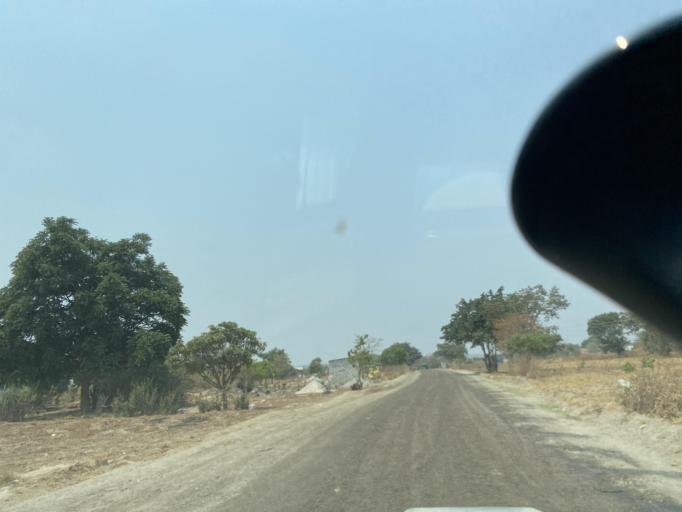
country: ZM
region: Lusaka
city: Lusaka
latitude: -15.5607
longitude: 28.4307
